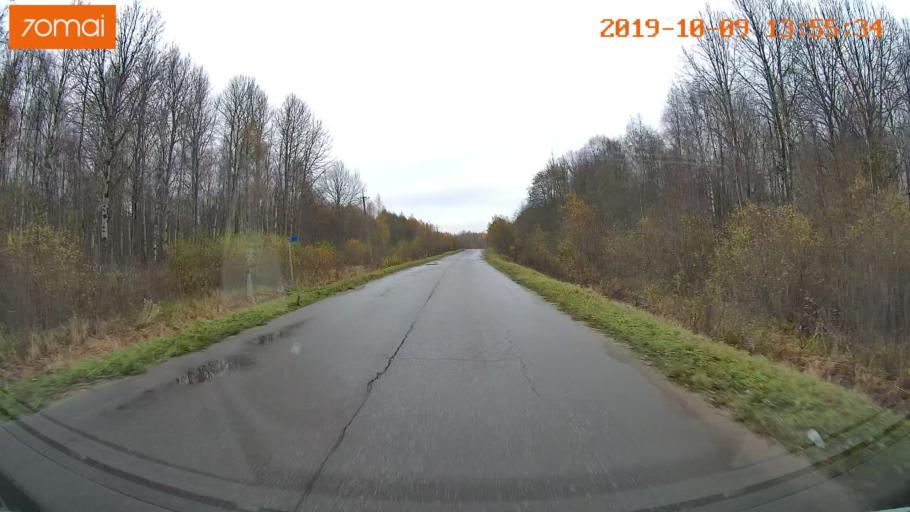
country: RU
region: Kostroma
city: Buy
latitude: 58.4253
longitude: 41.2755
